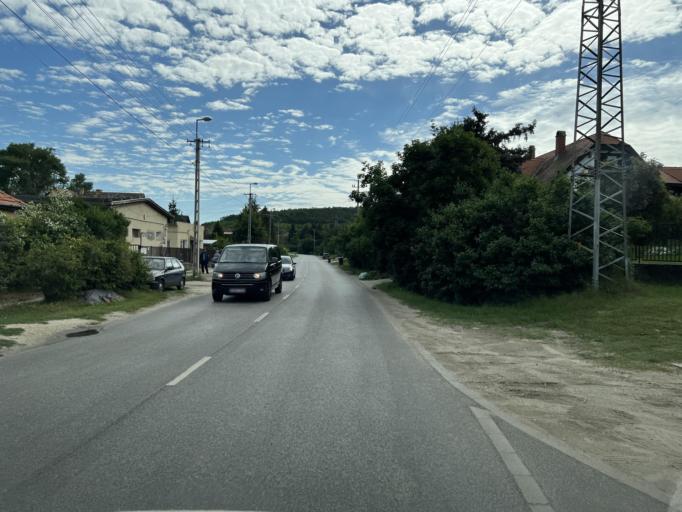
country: HU
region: Pest
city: Pecel
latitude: 47.4912
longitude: 19.3482
